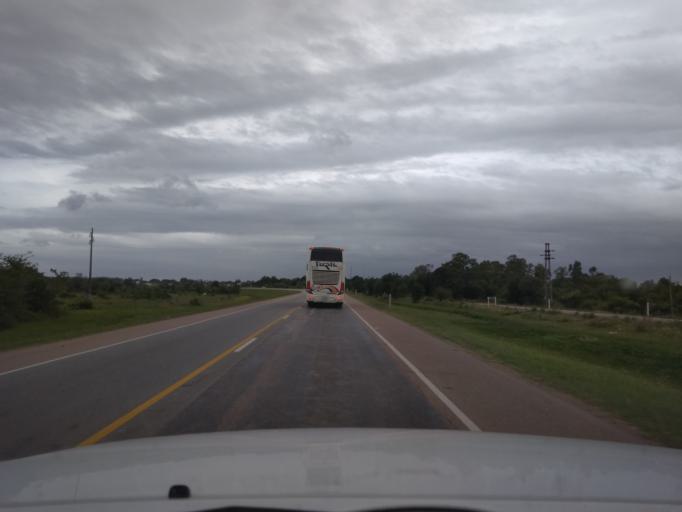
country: UY
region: Canelones
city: Canelones
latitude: -34.5038
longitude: -56.2815
